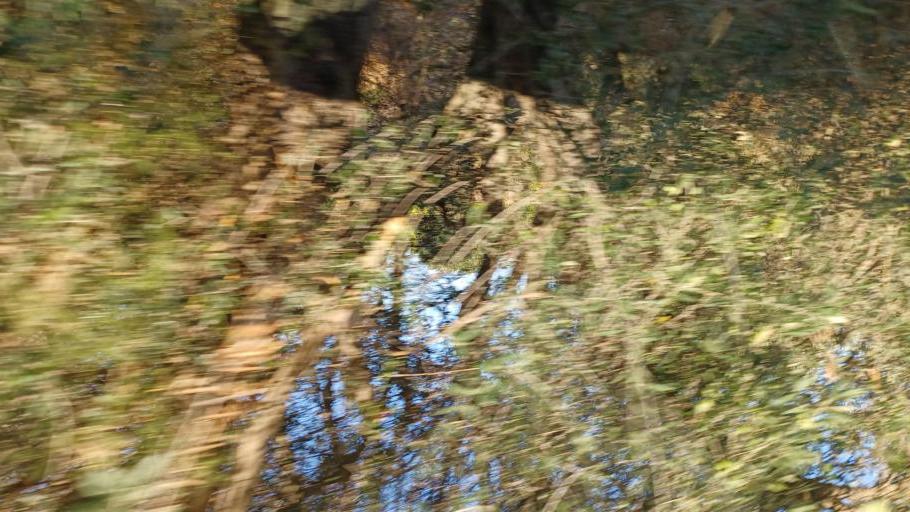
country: CY
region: Pafos
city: Polis
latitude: 34.9802
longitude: 32.4588
